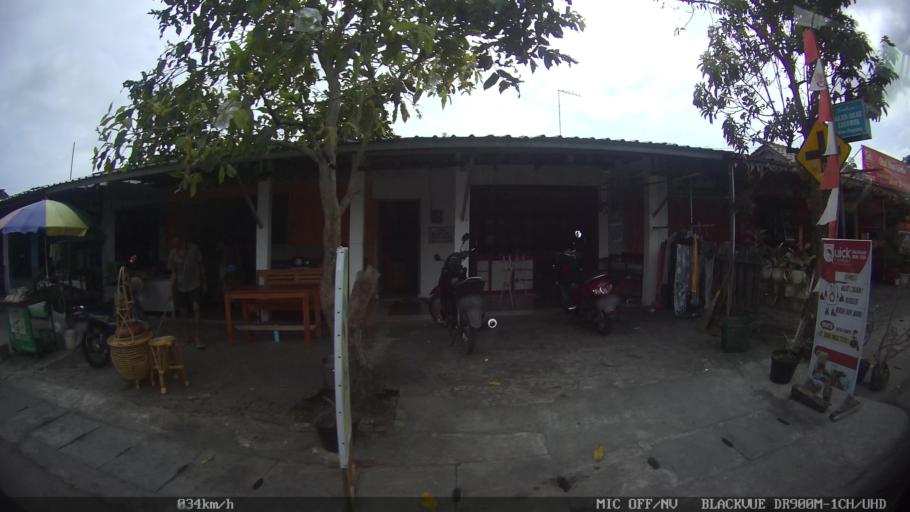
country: ID
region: Daerah Istimewa Yogyakarta
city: Depok
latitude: -7.8071
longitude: 110.4612
